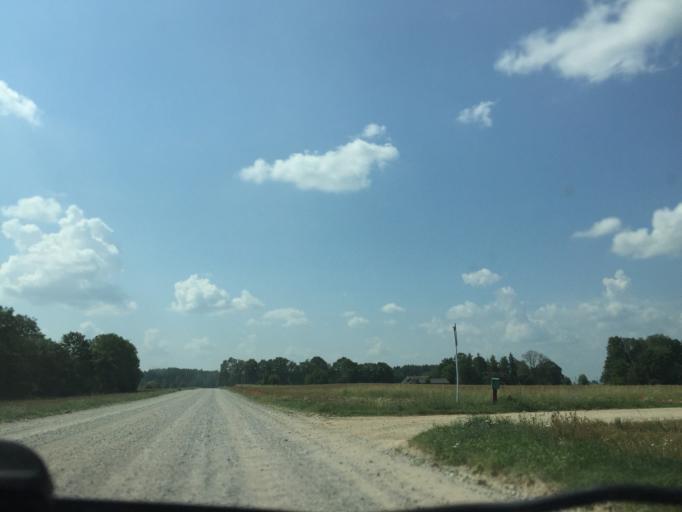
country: LV
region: Tervete
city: Zelmeni
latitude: 56.3920
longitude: 23.3139
